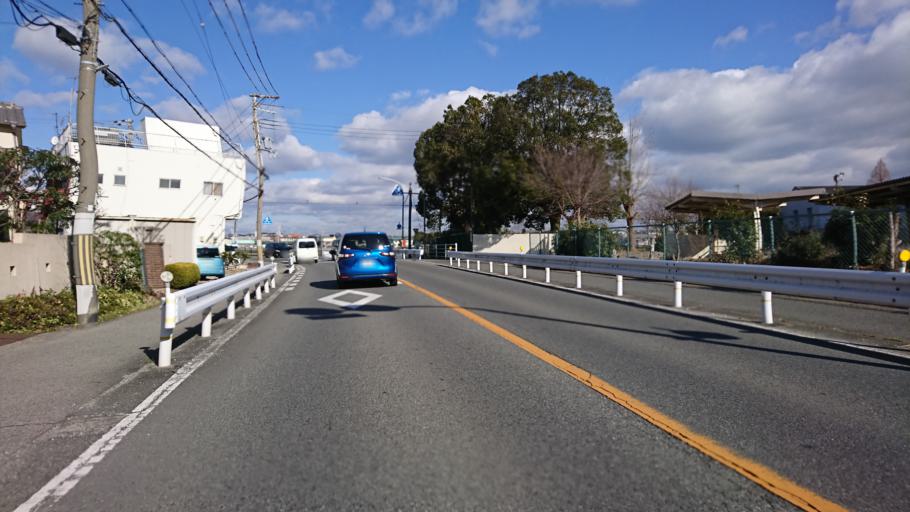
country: JP
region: Hyogo
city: Kakogawacho-honmachi
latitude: 34.7544
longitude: 134.8736
